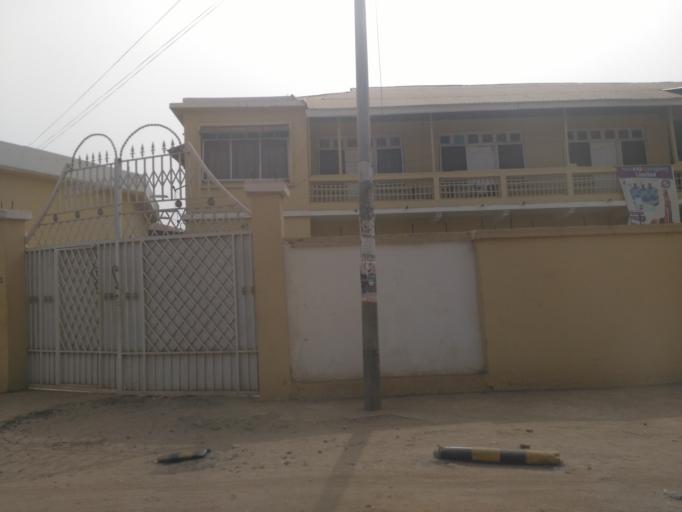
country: GH
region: Ashanti
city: Kumasi
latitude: 6.7055
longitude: -1.6253
